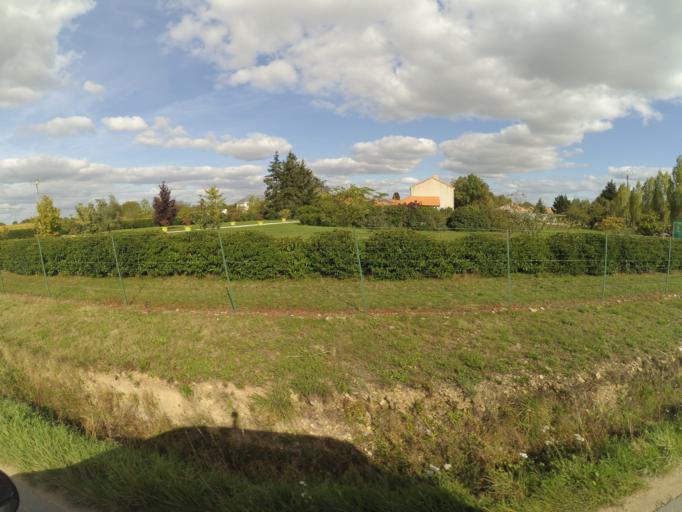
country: FR
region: Pays de la Loire
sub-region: Departement de la Loire-Atlantique
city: Saint-Julien-de-Concelles
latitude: 47.2344
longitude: -1.3838
